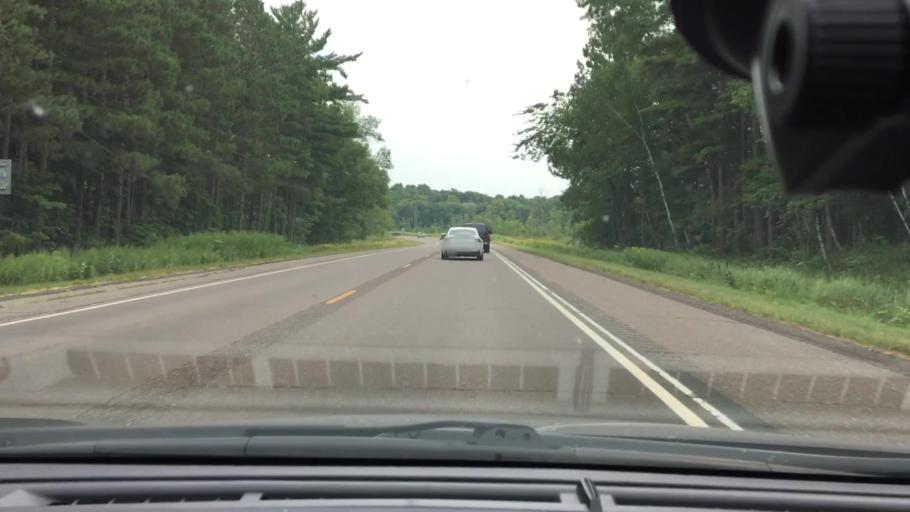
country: US
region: Minnesota
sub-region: Mille Lacs County
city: Vineland
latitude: 46.1444
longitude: -93.7206
